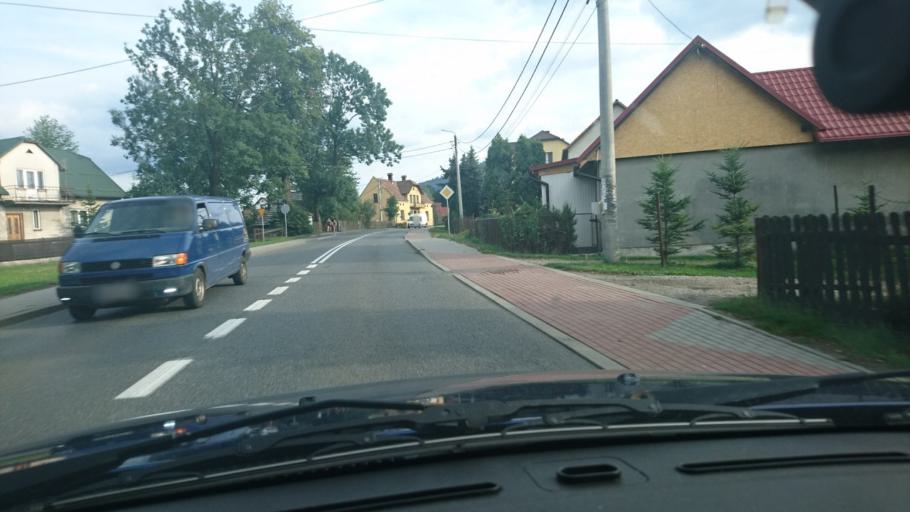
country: PL
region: Silesian Voivodeship
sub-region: Powiat zywiecki
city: Milowka
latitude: 49.5627
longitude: 19.0872
